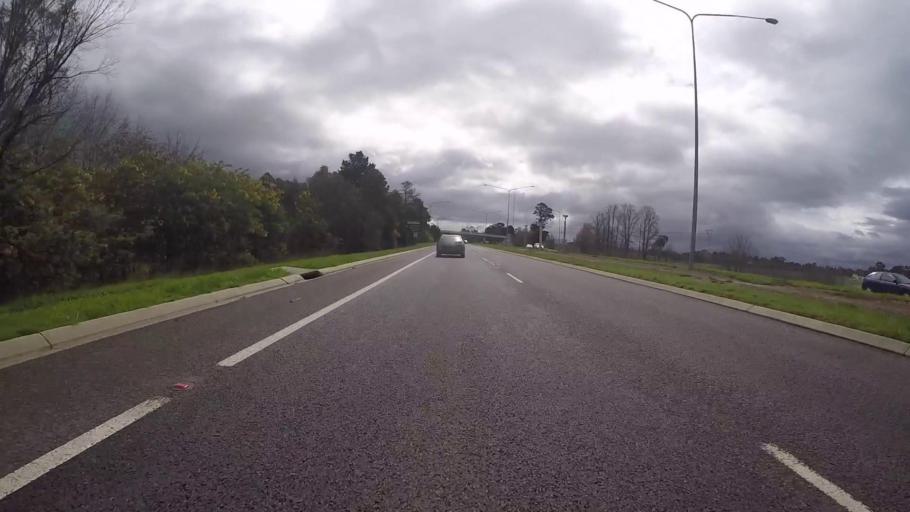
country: AU
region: Australian Capital Territory
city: Kaleen
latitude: -35.2287
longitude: 149.1236
